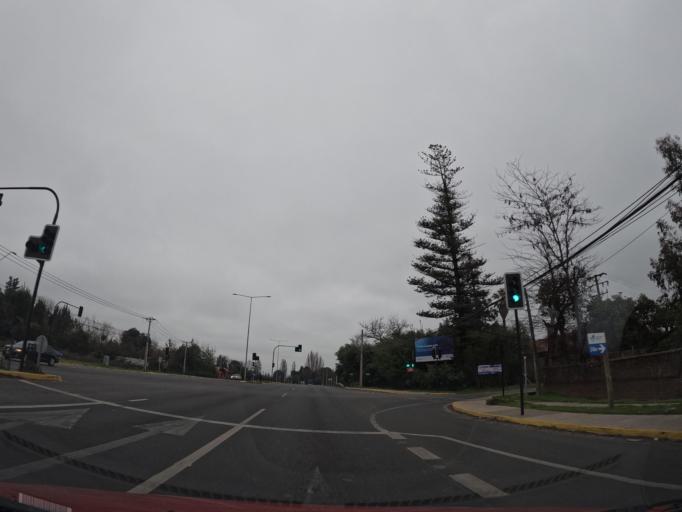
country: CL
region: Maule
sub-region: Provincia de Talca
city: Talca
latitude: -35.4471
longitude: -71.6025
